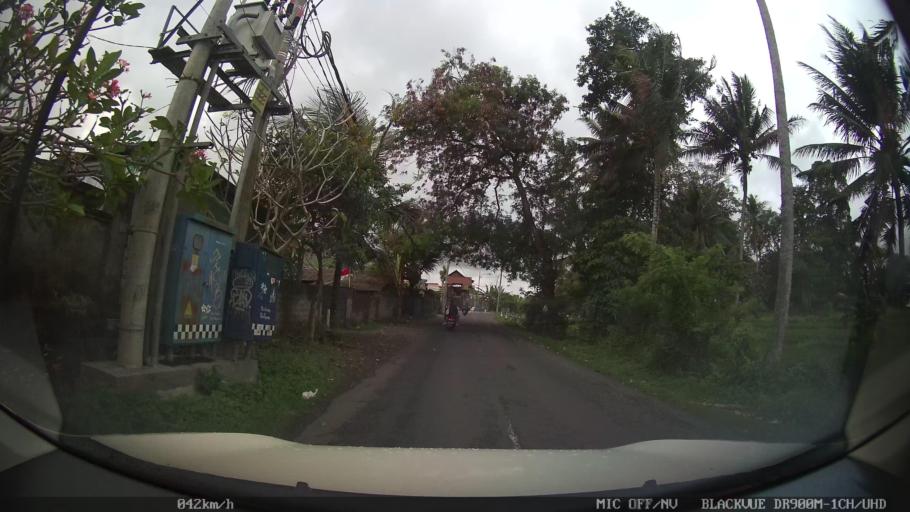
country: ID
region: Bali
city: Banjar Cemenggon
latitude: -8.5508
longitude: 115.1941
